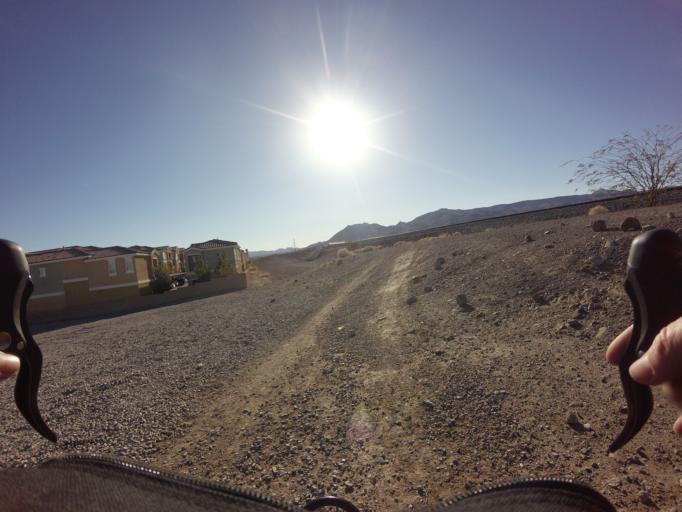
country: US
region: Nevada
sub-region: Clark County
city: Whitney
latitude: 36.0418
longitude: -115.0543
